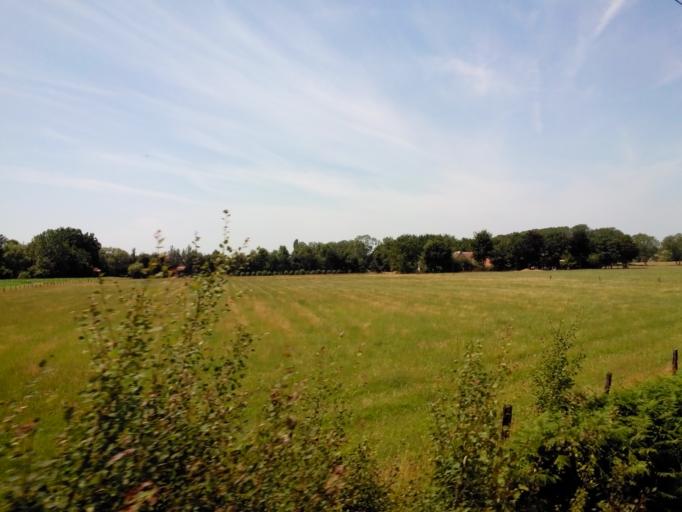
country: BE
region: Flanders
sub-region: Provincie Antwerpen
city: Lier
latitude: 51.1339
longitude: 4.6033
